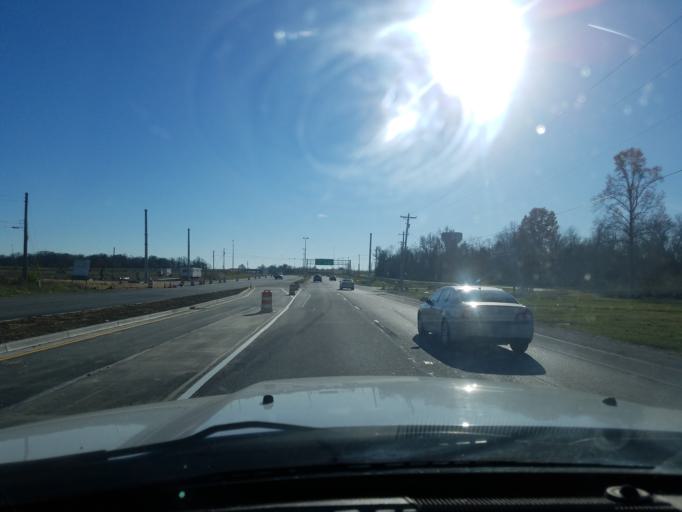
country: US
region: Indiana
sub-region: Clark County
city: Oak Park
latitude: 38.3504
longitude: -85.7048
